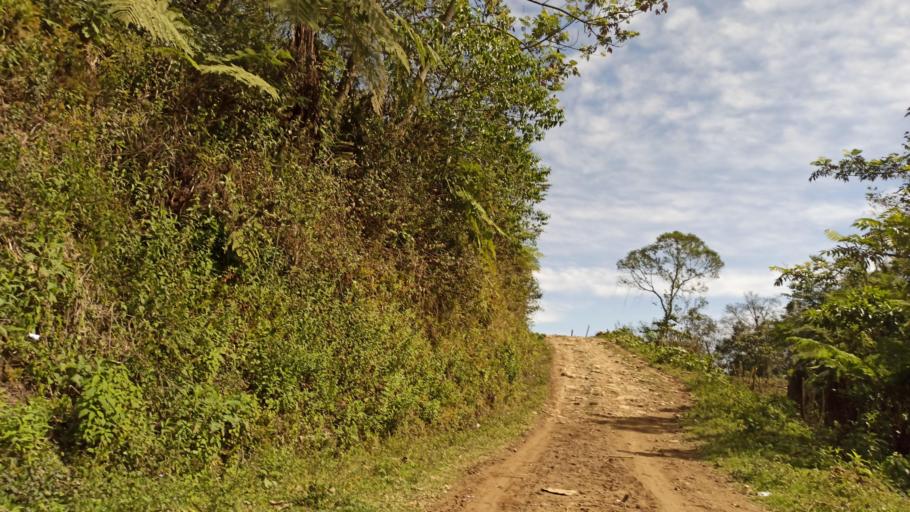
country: MX
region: Veracruz
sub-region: La Perla
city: Metlac Hernandez (Metlac Primero)
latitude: 18.9707
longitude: -97.1018
